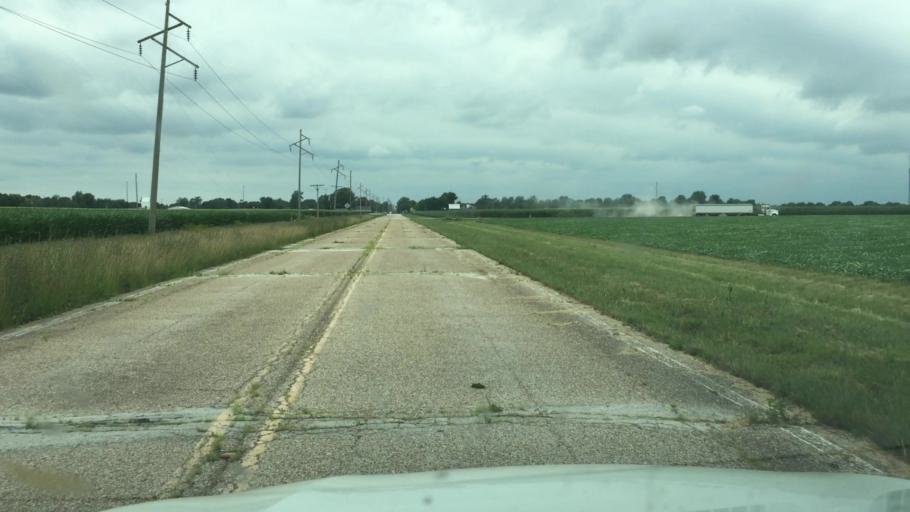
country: US
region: Illinois
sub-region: Hancock County
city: Carthage
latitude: 40.4159
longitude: -91.1090
